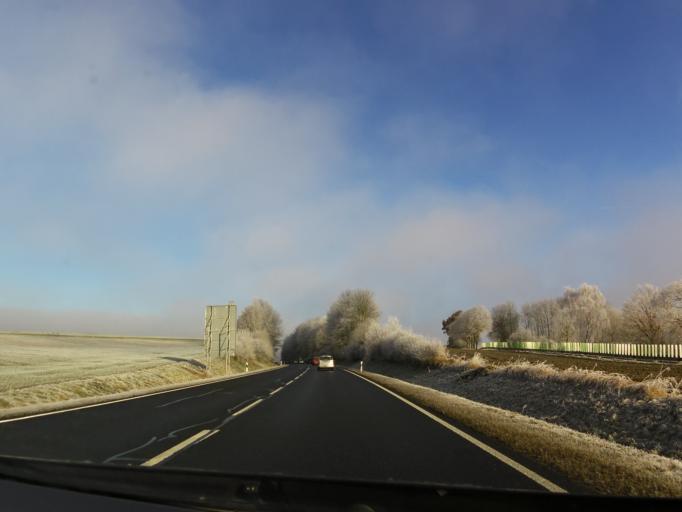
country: DE
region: Bavaria
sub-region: Upper Franconia
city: Arzberg
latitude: 50.0490
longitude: 12.1684
